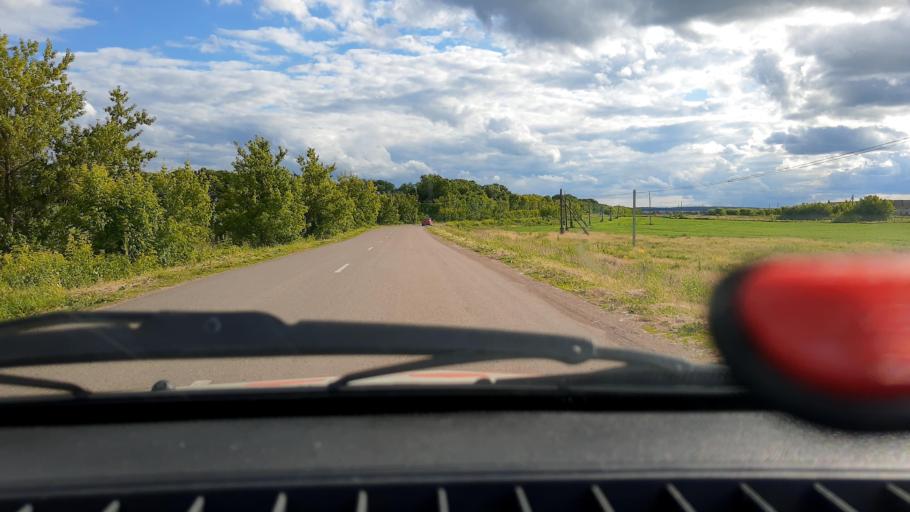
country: RU
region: Bashkortostan
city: Kabakovo
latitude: 54.5135
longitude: 55.9429
